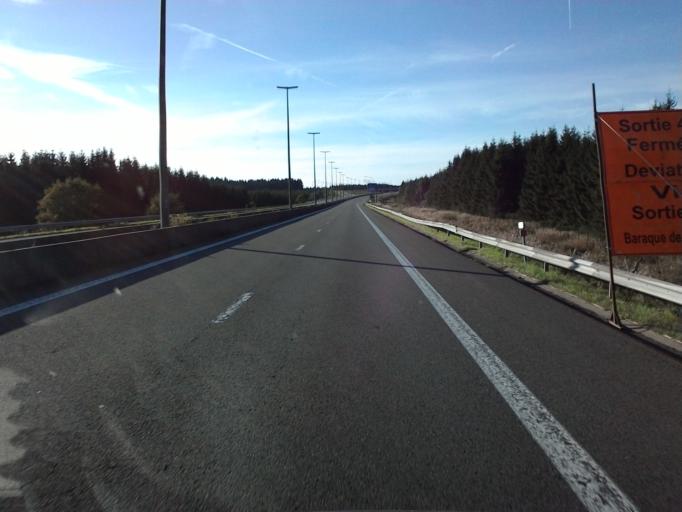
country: BE
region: Wallonia
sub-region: Province de Liege
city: Lierneux
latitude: 50.2442
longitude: 5.7422
